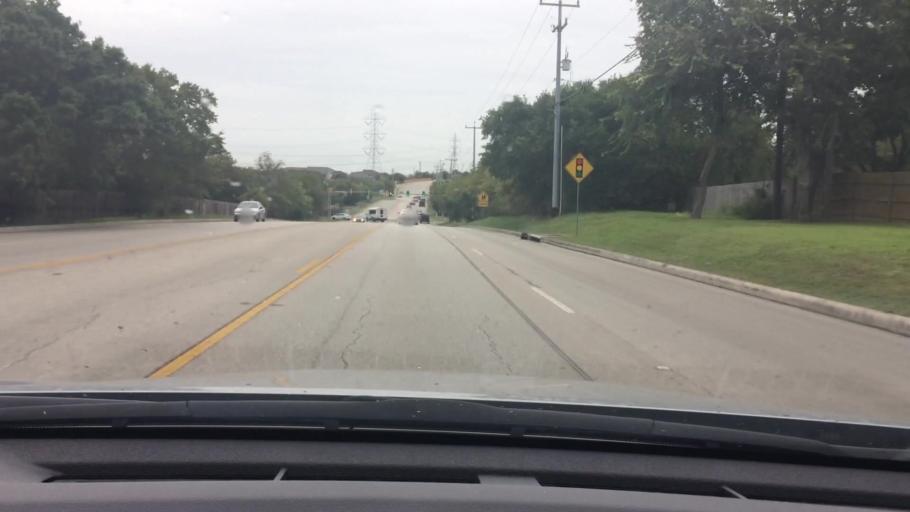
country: US
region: Texas
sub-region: Bexar County
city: Windcrest
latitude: 29.5291
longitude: -98.3509
